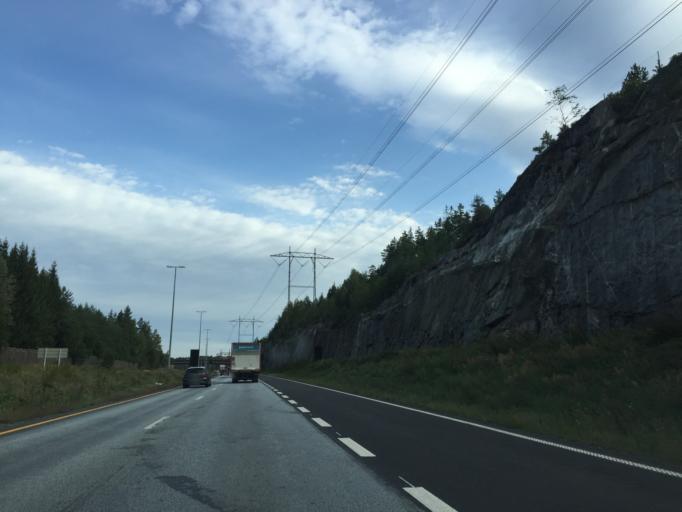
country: NO
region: Akershus
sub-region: Oppegard
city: Kolbotn
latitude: 59.8035
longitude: 10.8428
